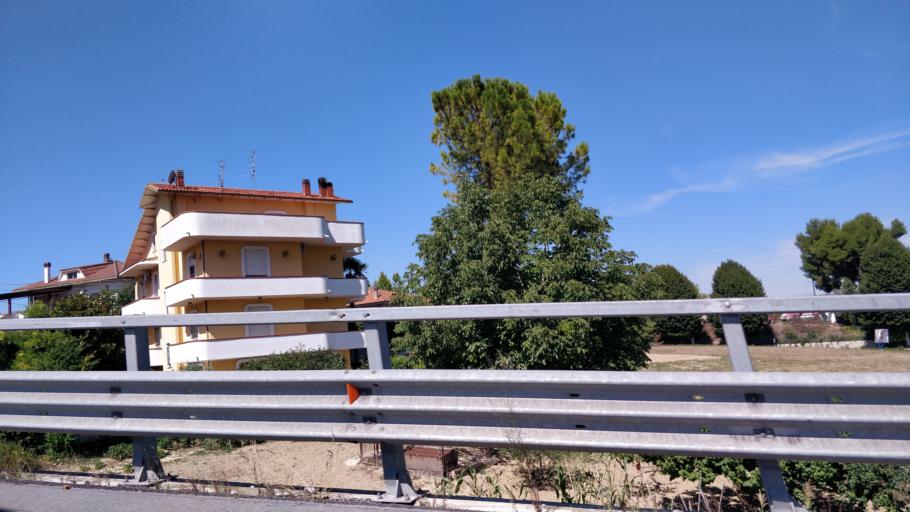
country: IT
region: Abruzzo
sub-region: Provincia di Chieti
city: Chieti
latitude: 42.3929
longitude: 14.1626
